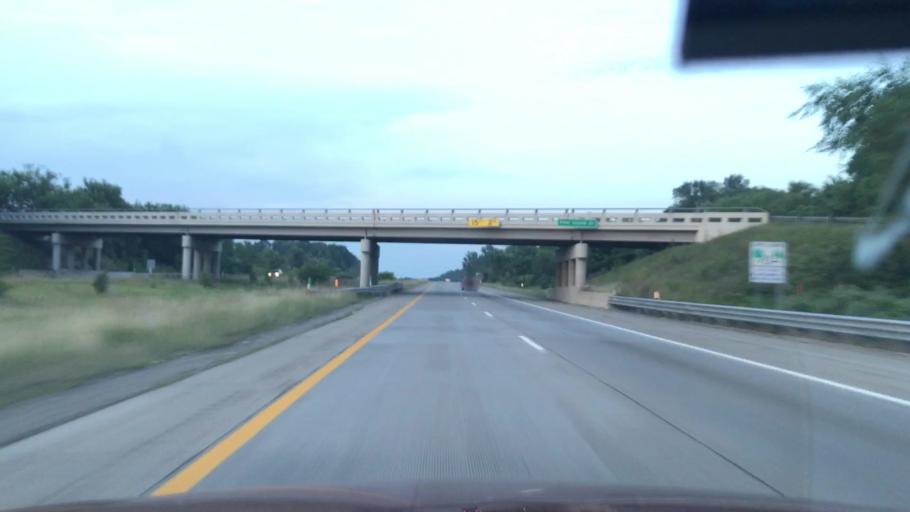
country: US
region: Michigan
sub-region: Kent County
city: Comstock Park
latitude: 43.0687
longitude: -85.6548
